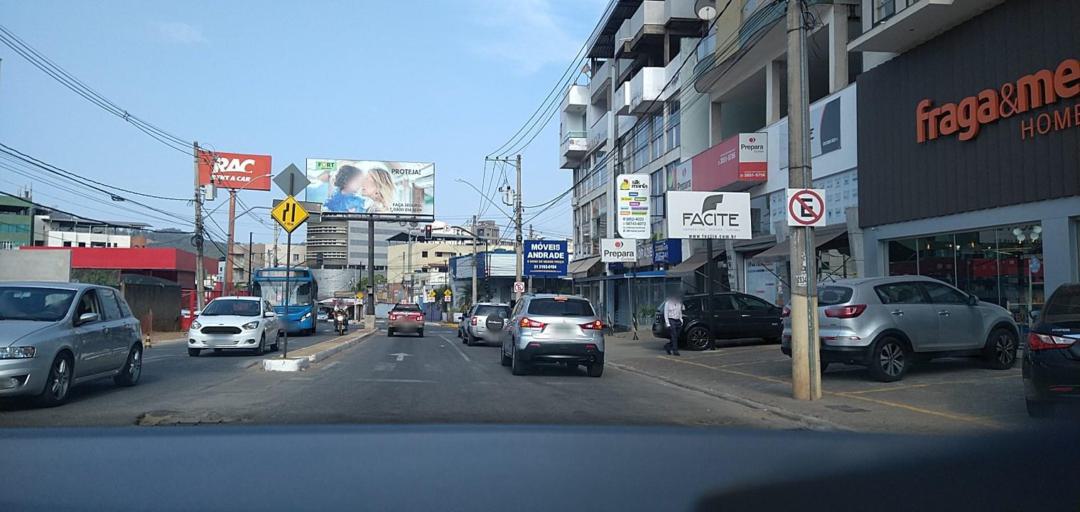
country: BR
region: Minas Gerais
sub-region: Joao Monlevade
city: Joao Monlevade
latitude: -19.8082
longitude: -43.1818
